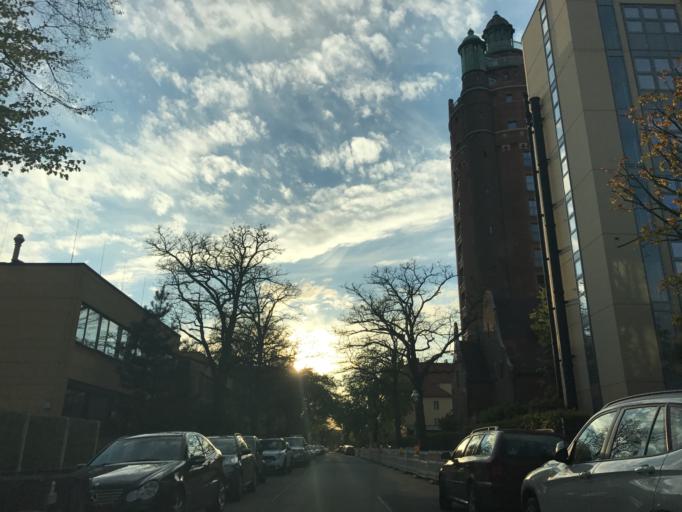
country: DE
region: Berlin
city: Westend
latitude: 52.5193
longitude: 13.2690
